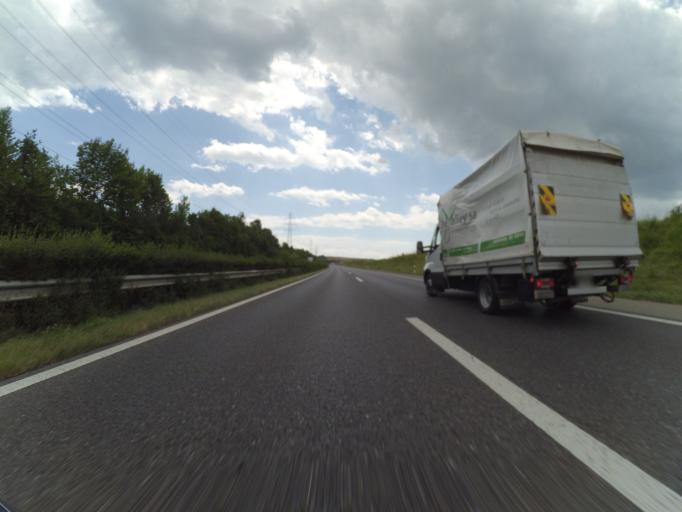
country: CH
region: Vaud
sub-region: Jura-Nord vaudois District
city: Bavois
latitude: 46.6907
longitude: 6.5735
